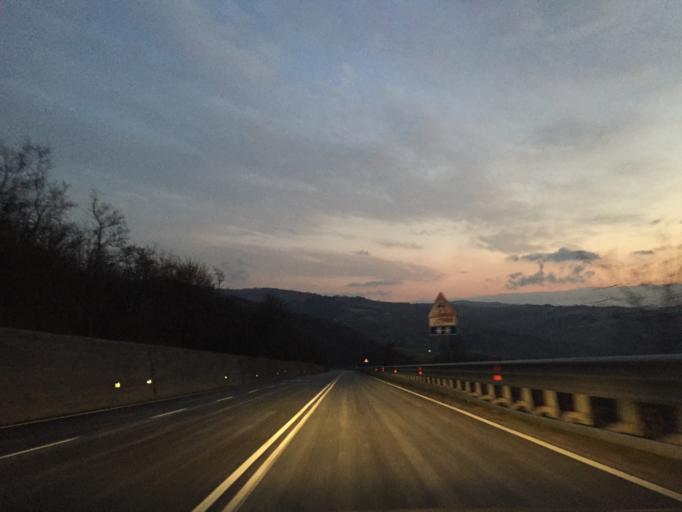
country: IT
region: Apulia
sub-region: Provincia di Foggia
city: Volturino
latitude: 41.4665
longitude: 15.0943
